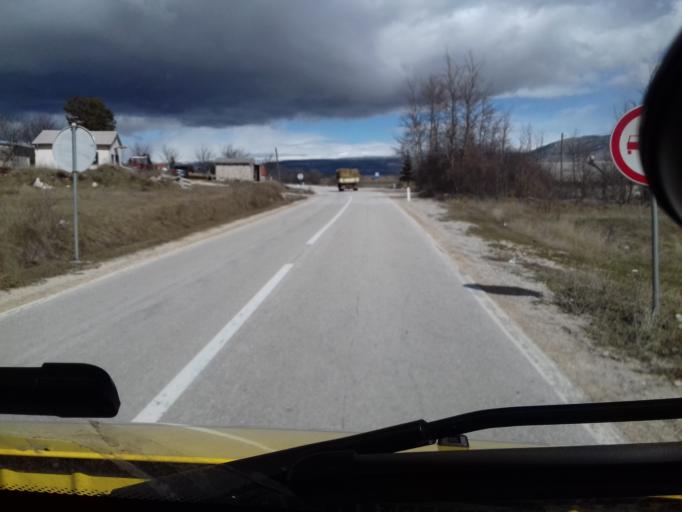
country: BA
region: Federation of Bosnia and Herzegovina
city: Dreznica
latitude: 43.5958
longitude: 17.2736
